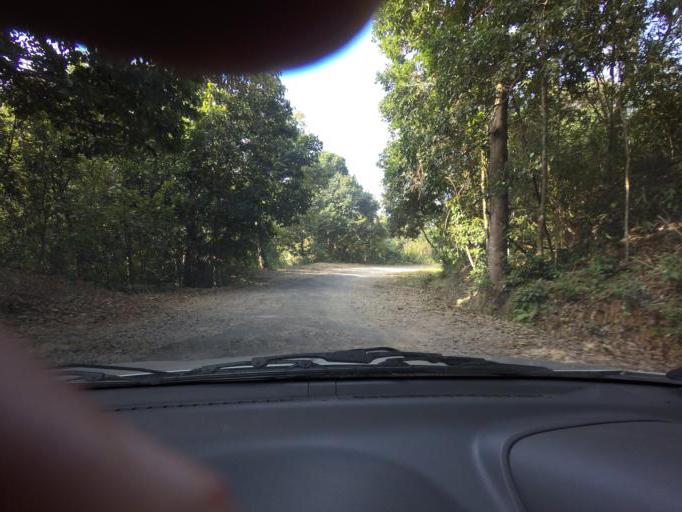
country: IN
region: Karnataka
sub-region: Kodagu
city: Somvarpet
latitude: 12.7127
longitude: 75.6907
